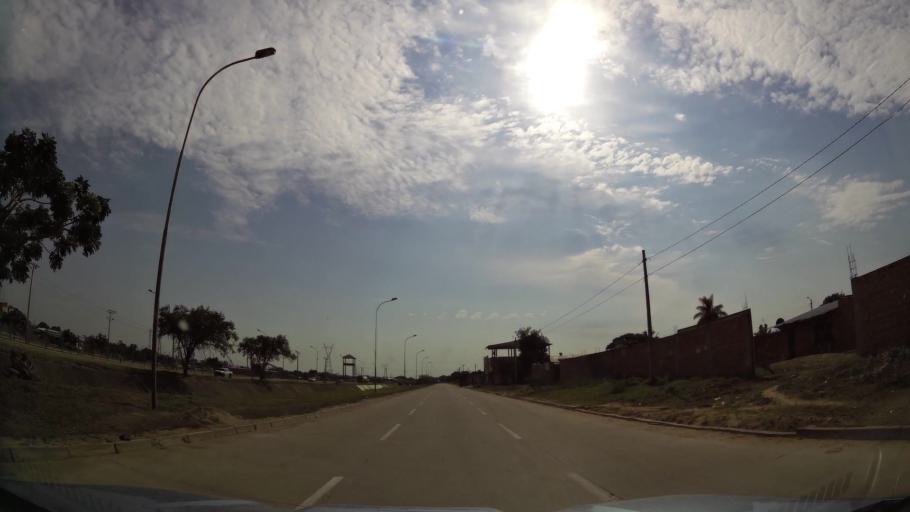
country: BO
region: Santa Cruz
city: Santa Cruz de la Sierra
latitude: -17.7306
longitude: -63.1370
